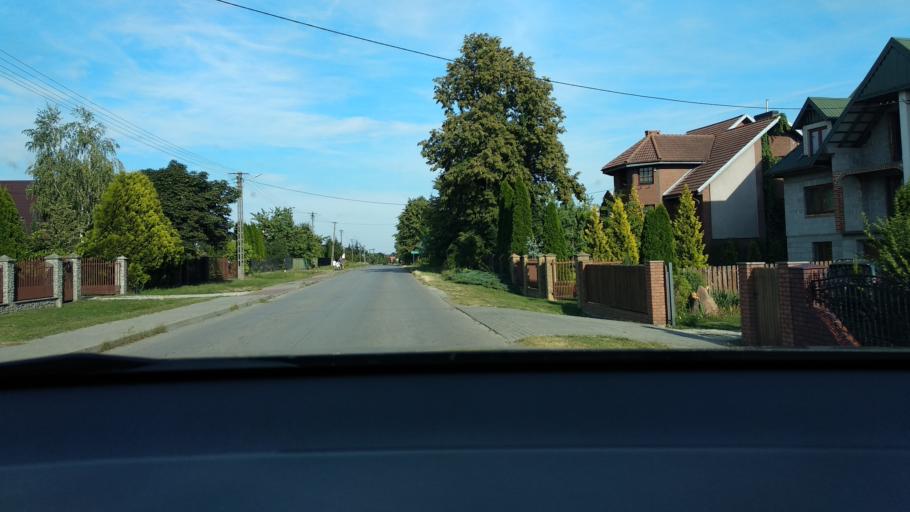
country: PL
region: Masovian Voivodeship
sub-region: Powiat pultuski
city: Obryte
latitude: 52.7140
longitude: 21.1883
